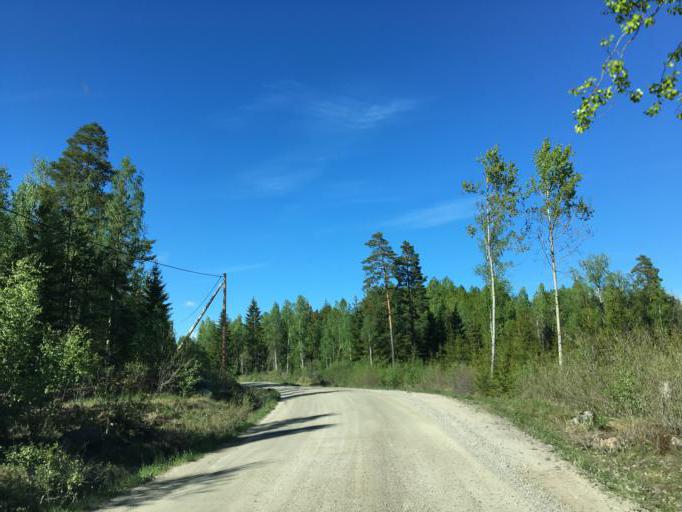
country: SE
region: Soedermanland
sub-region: Eskilstuna Kommun
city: Kvicksund
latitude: 59.3676
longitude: 16.2642
